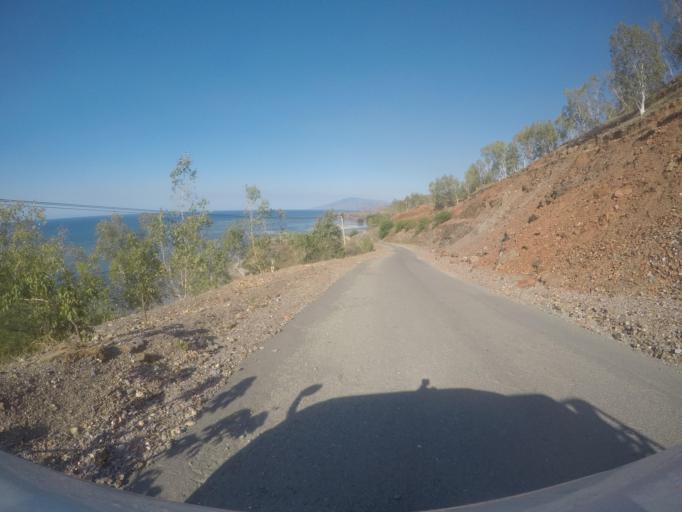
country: TL
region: Dili
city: Dili
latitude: -8.5267
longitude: 125.6289
